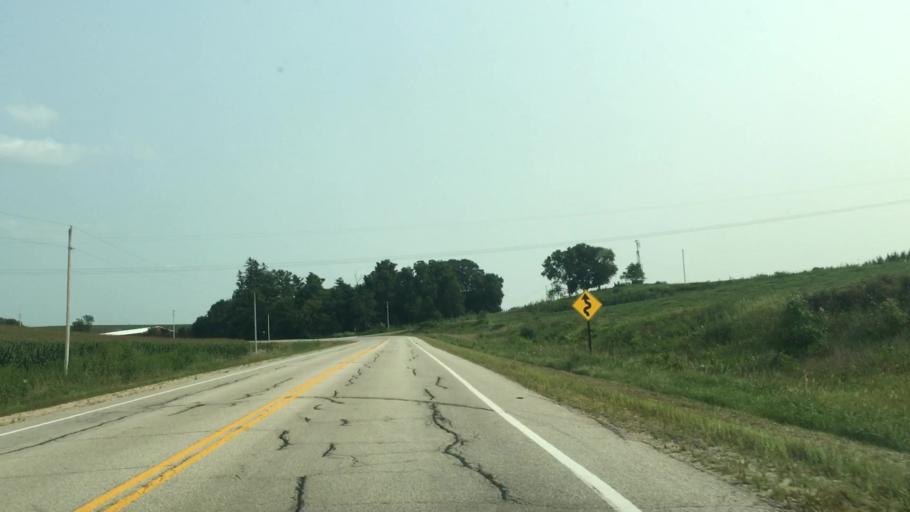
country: US
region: Minnesota
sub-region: Fillmore County
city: Preston
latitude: 43.6939
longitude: -91.9524
